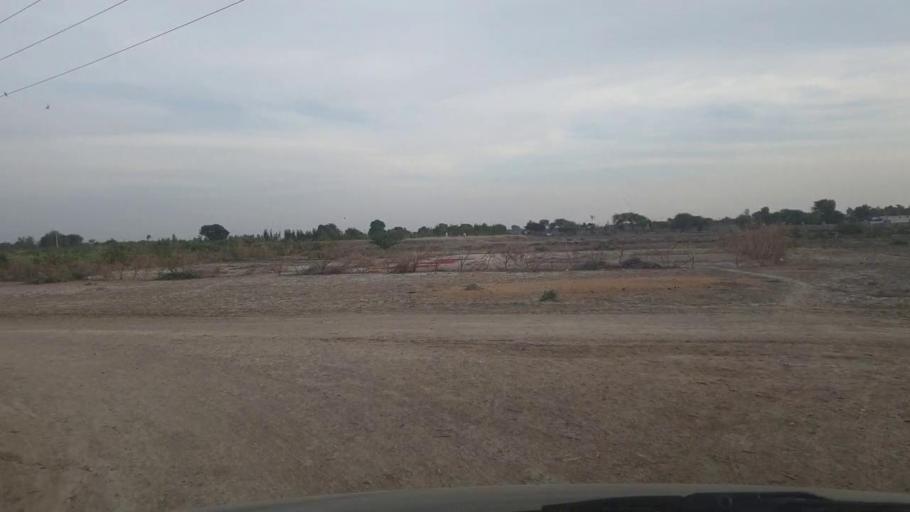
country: PK
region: Sindh
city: Kunri
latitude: 25.2562
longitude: 69.5418
